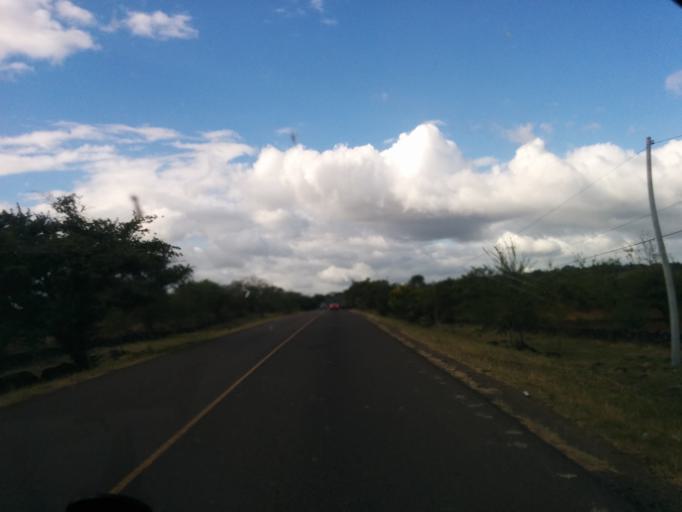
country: NI
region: Esteli
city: Esteli
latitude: 13.1972
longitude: -86.3739
